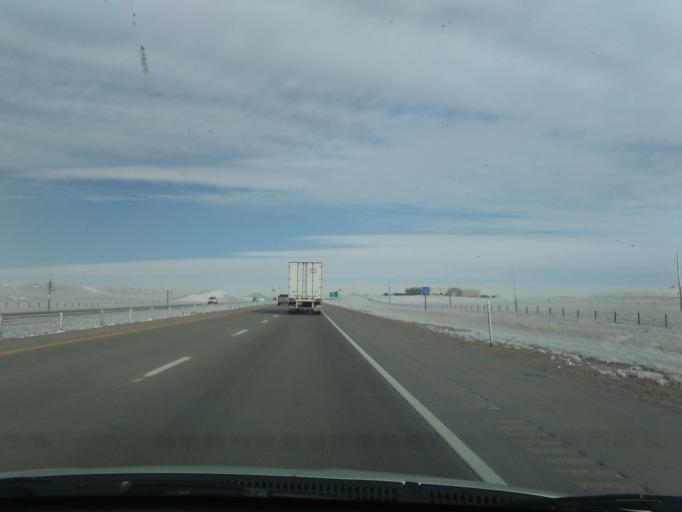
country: US
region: Wyoming
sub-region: Laramie County
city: South Greeley
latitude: 41.0268
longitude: -104.9008
